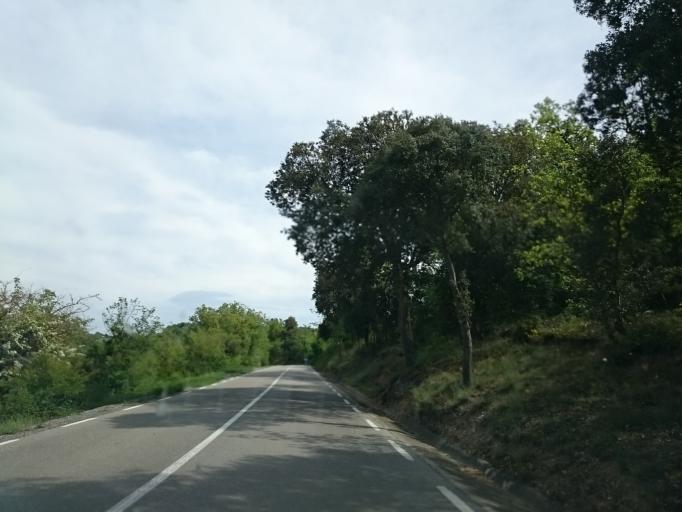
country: ES
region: Catalonia
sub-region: Provincia de Barcelona
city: Calaf
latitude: 41.7336
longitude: 1.4893
